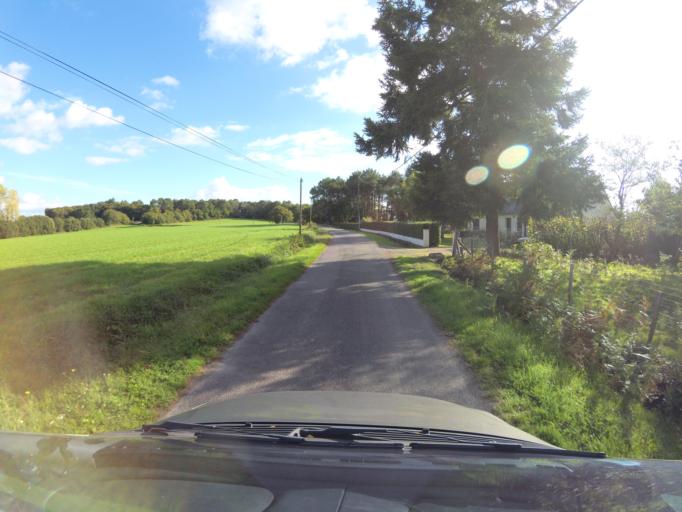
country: FR
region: Brittany
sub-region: Departement du Morbihan
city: Peillac
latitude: 47.7219
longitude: -2.2333
